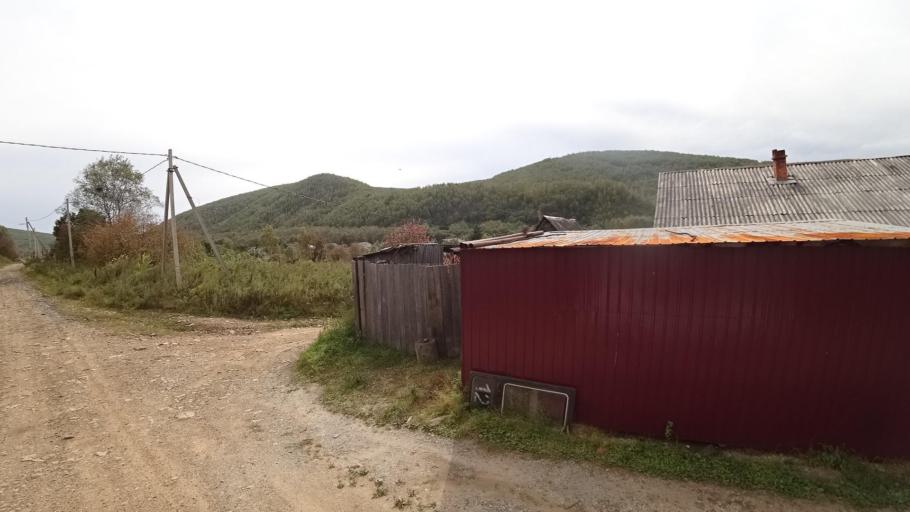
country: RU
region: Jewish Autonomous Oblast
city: Khingansk
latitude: 49.1244
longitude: 131.2057
